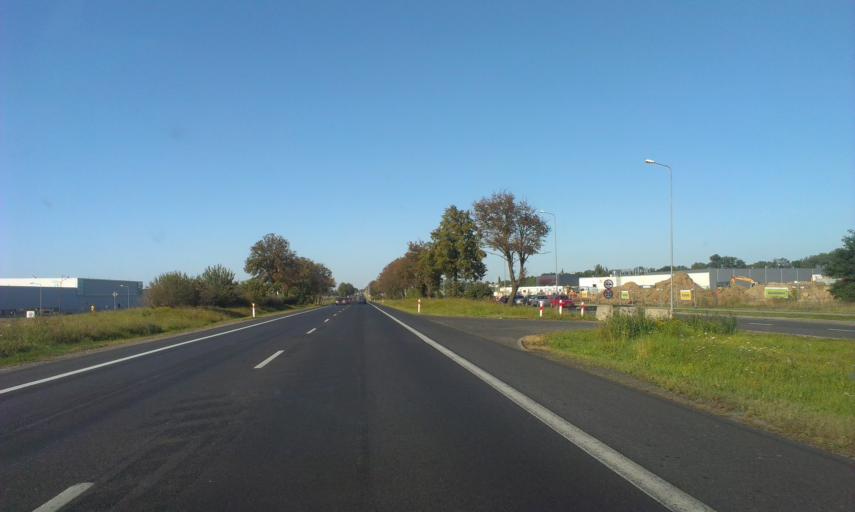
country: PL
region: Kujawsko-Pomorskie
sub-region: Powiat torunski
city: Lysomice
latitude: 53.1037
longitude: 18.6232
